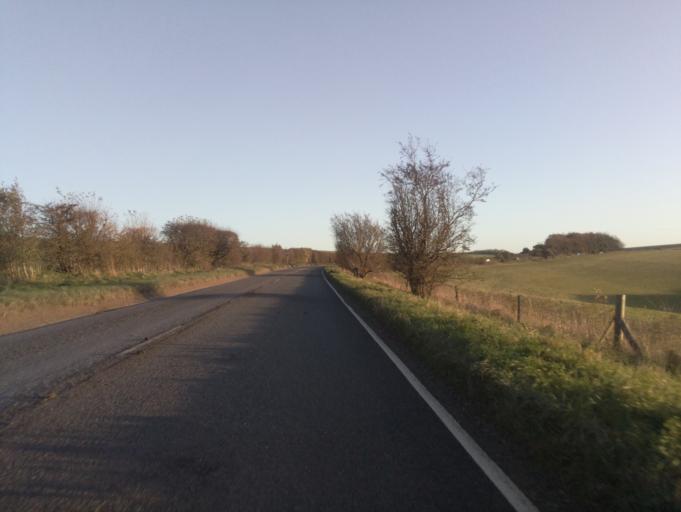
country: GB
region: England
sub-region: Wiltshire
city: Bishopstrow
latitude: 51.1480
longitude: -2.1622
